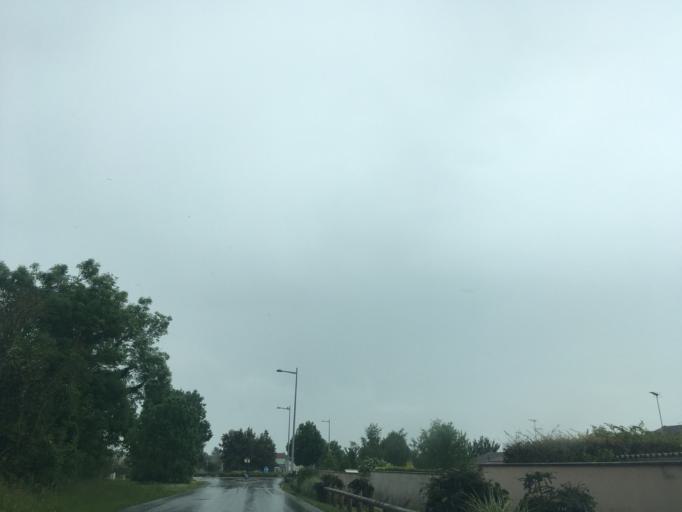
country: FR
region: Poitou-Charentes
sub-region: Departement de la Charente
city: Chateaubernard
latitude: 45.6759
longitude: -0.3093
